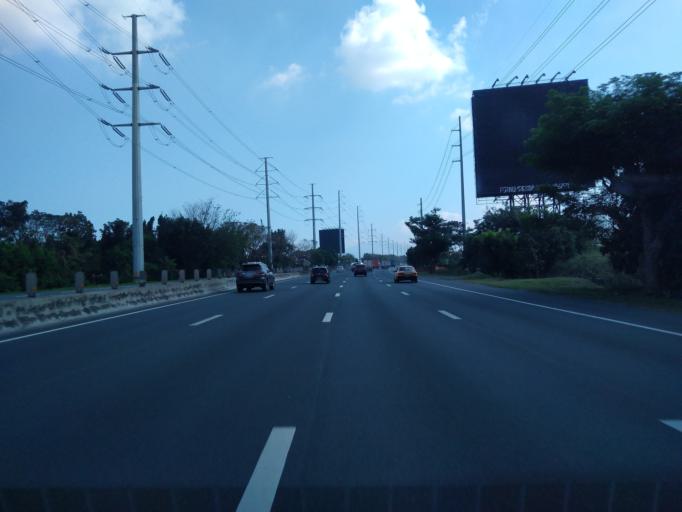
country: PH
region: Calabarzon
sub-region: Province of Cavite
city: Carmona
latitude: 14.3009
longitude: 121.0802
